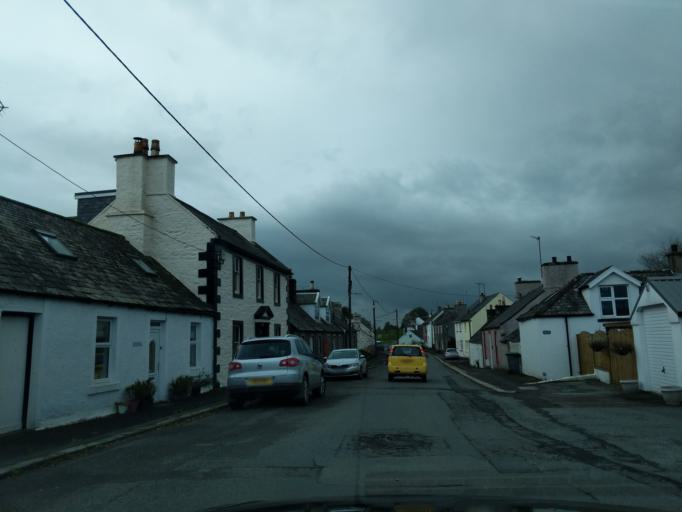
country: GB
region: Scotland
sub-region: Dumfries and Galloway
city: Castle Douglas
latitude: 54.9177
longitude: -3.9620
